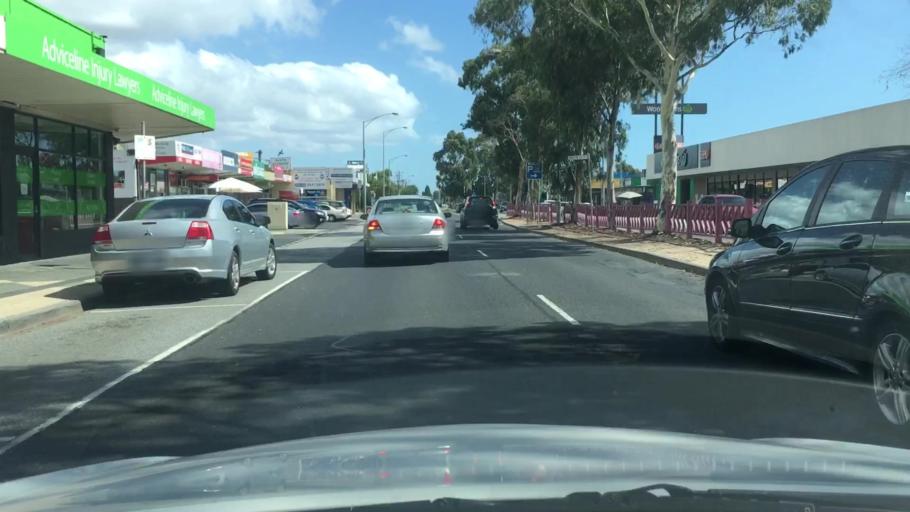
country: AU
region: Victoria
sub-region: Greater Dandenong
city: Springvale
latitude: -37.9530
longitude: 145.1522
